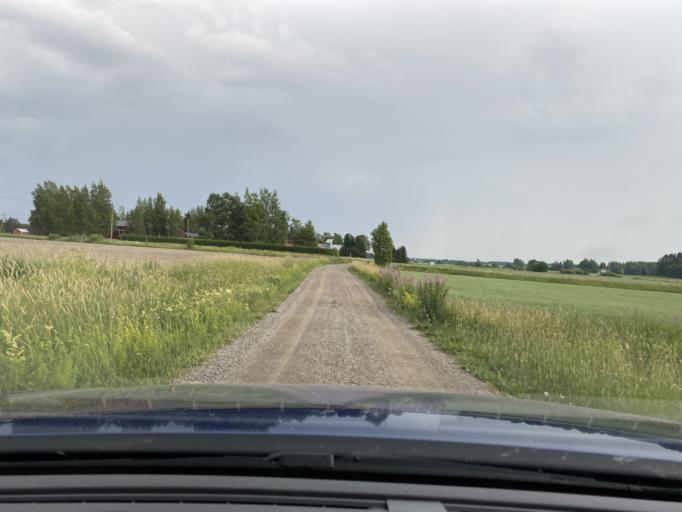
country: FI
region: Satakunta
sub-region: Rauma
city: Eura
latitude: 61.1577
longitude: 22.0951
